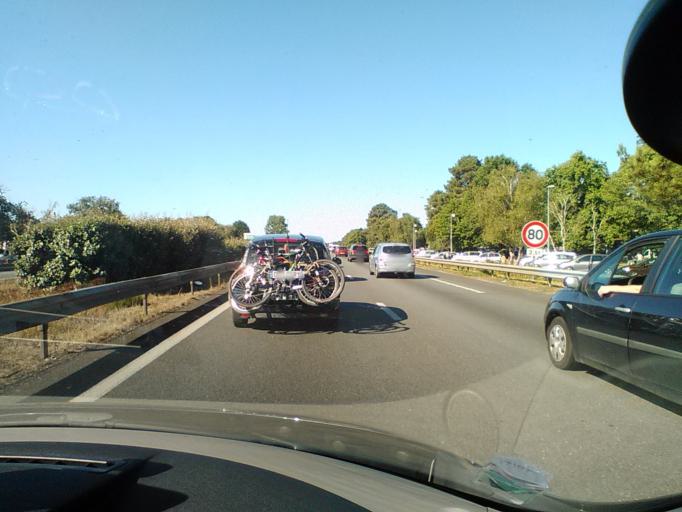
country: FR
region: Aquitaine
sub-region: Departement de la Gironde
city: Saint-Aubin-de-Medoc
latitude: 44.7461
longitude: -0.7017
